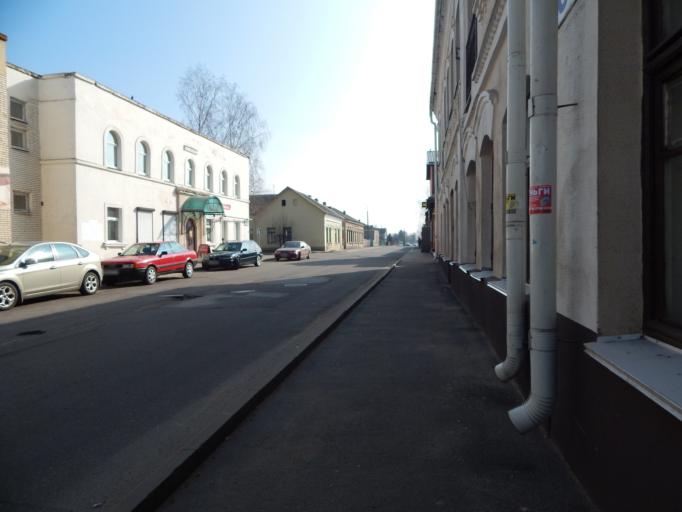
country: BY
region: Minsk
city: Horad Barysaw
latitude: 54.2462
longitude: 28.5069
